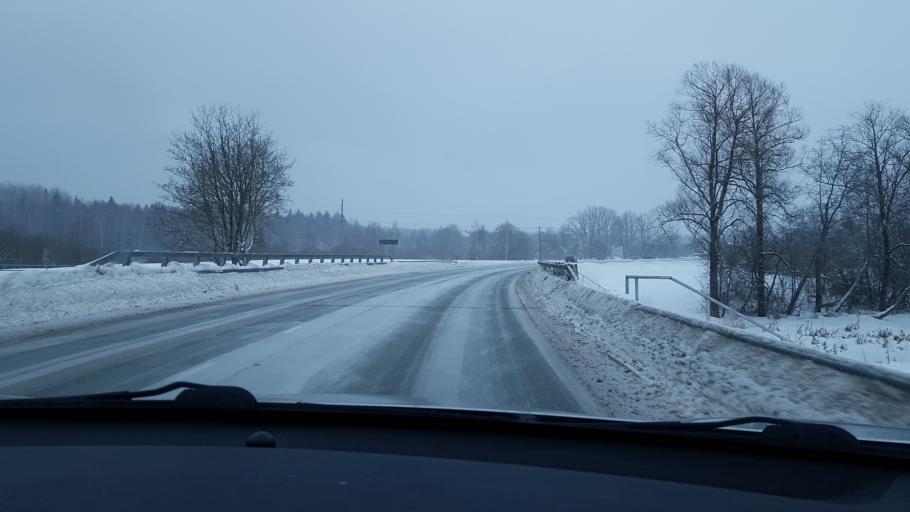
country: EE
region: Jaervamaa
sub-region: Tueri vald
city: Sarevere
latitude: 58.7888
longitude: 25.4216
